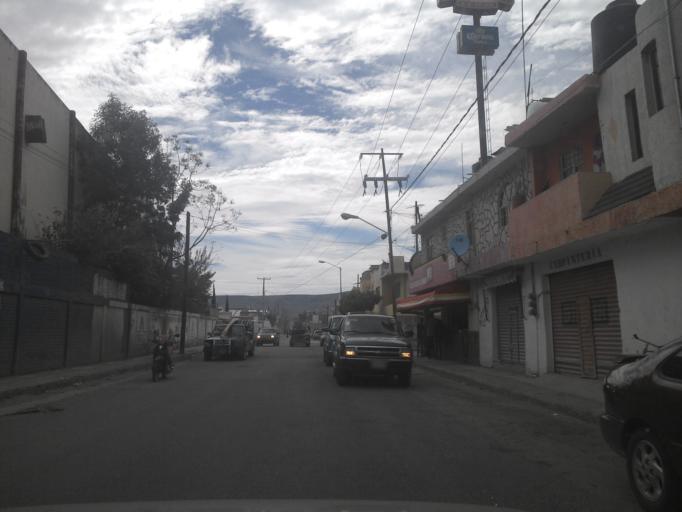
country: MX
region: Guanajuato
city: San Francisco del Rincon
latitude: 21.0104
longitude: -101.8511
